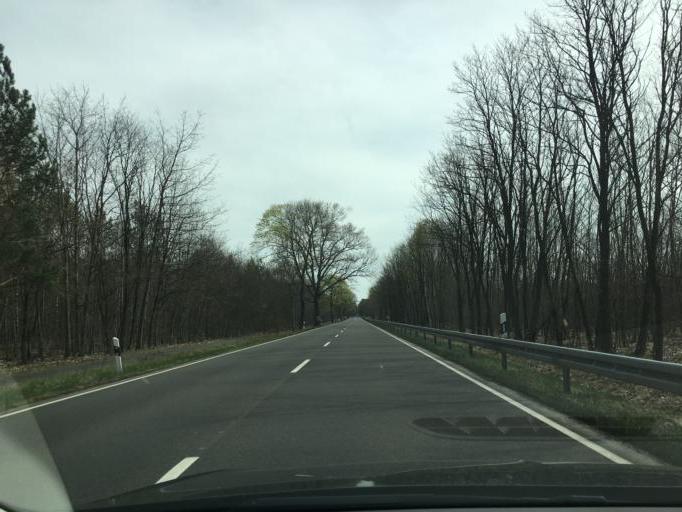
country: DE
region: Brandenburg
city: Spremberg
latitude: 51.5697
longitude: 14.4362
